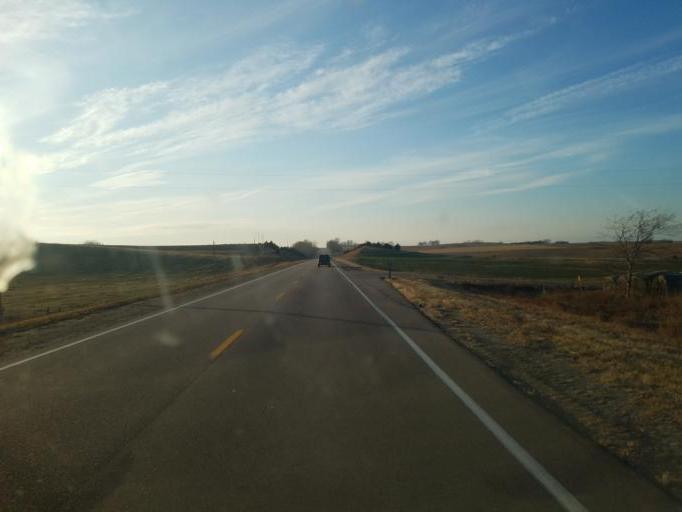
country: US
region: South Dakota
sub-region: Yankton County
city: Yankton
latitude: 42.7287
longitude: -97.4159
